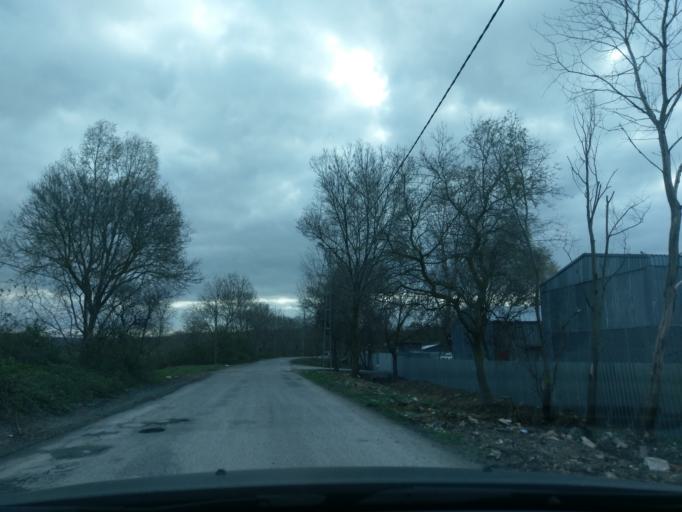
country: TR
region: Istanbul
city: Durusu
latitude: 41.2979
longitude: 28.6755
